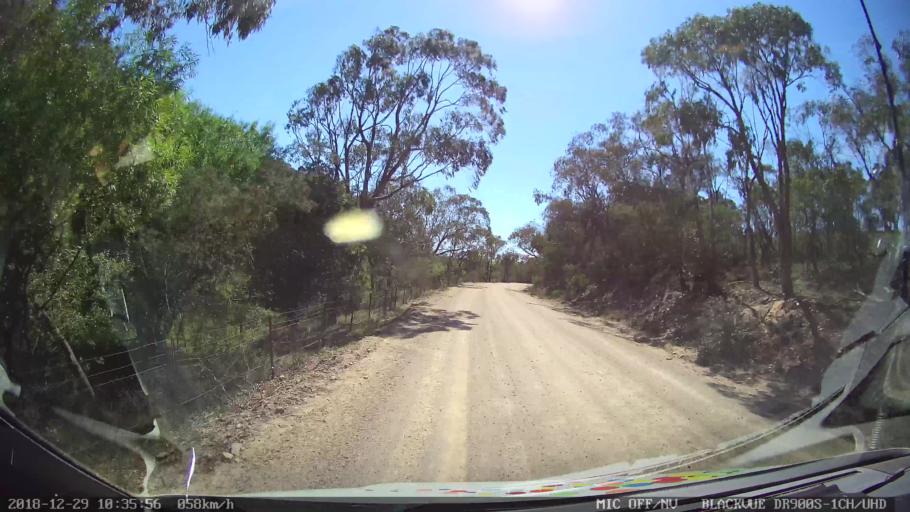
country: AU
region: New South Wales
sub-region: Yass Valley
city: Gundaroo
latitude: -34.9926
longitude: 149.4869
